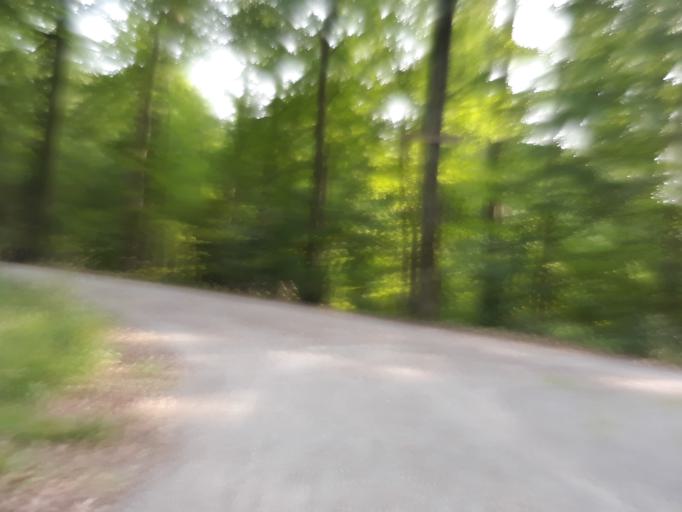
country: DE
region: Baden-Wuerttemberg
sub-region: Regierungsbezirk Stuttgart
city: Schonaich
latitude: 48.6711
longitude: 9.0422
